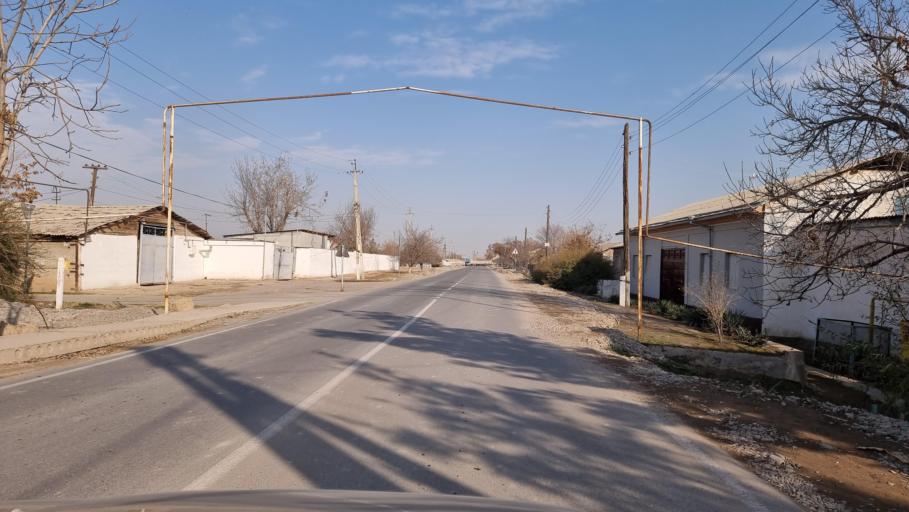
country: UZ
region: Toshkent
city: Urtaowul
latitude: 41.1880
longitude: 69.1209
